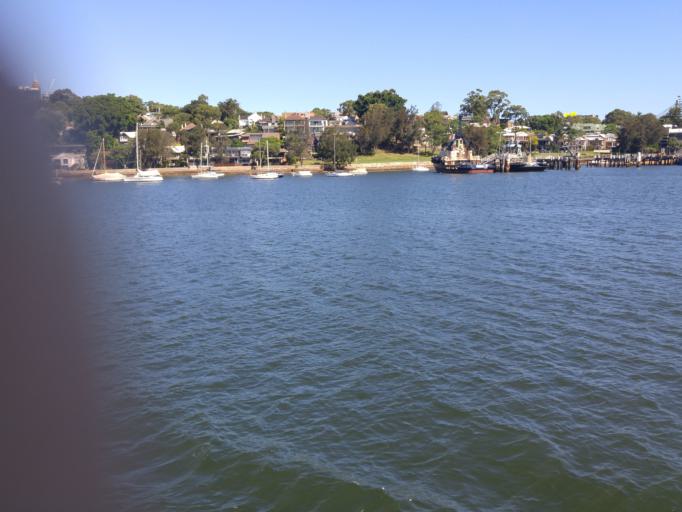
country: AU
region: New South Wales
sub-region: Leichhardt
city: Balmain East
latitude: -33.8538
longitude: 151.1889
